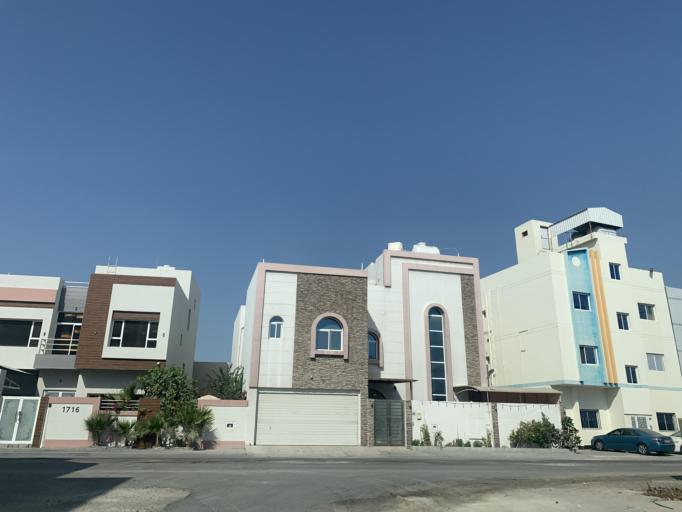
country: BH
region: Central Governorate
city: Madinat Hamad
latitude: 26.1301
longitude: 50.4874
